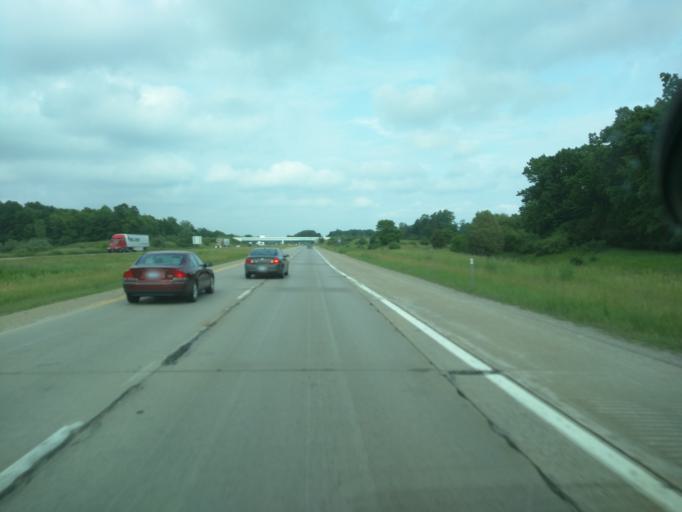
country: US
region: Michigan
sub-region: Clinton County
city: Bath
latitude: 42.8023
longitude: -84.4903
